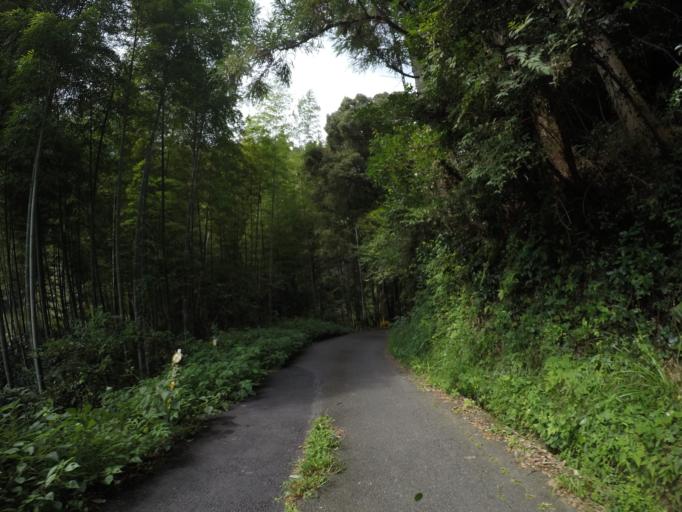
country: JP
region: Shizuoka
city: Shimada
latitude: 34.8768
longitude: 138.1758
